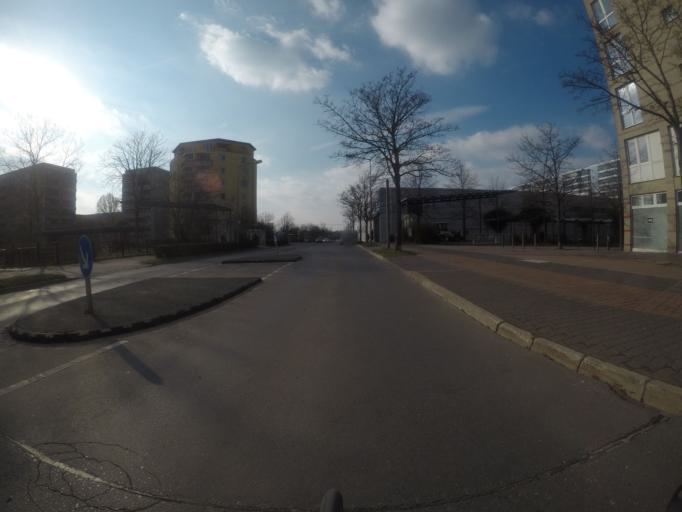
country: DE
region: Berlin
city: Altglienicke
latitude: 52.4016
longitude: 13.5256
